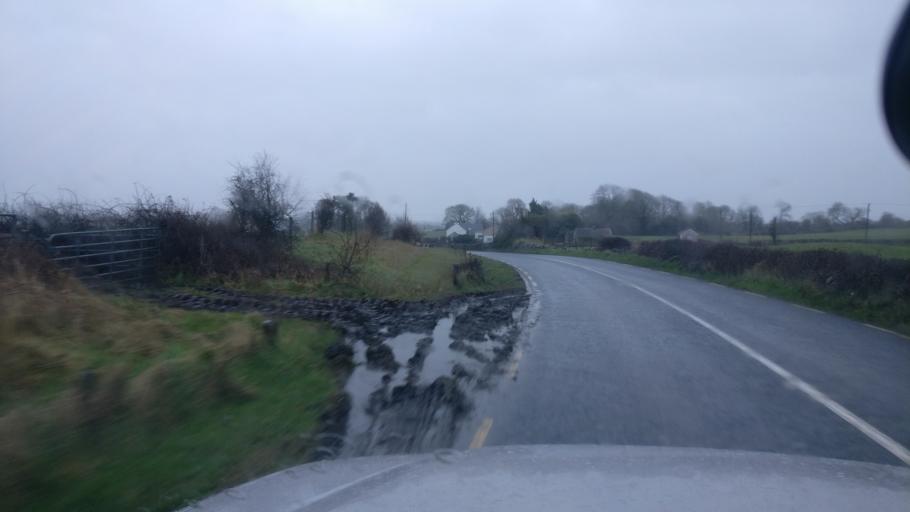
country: IE
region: Connaught
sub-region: County Galway
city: Ballinasloe
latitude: 53.2796
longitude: -8.2203
